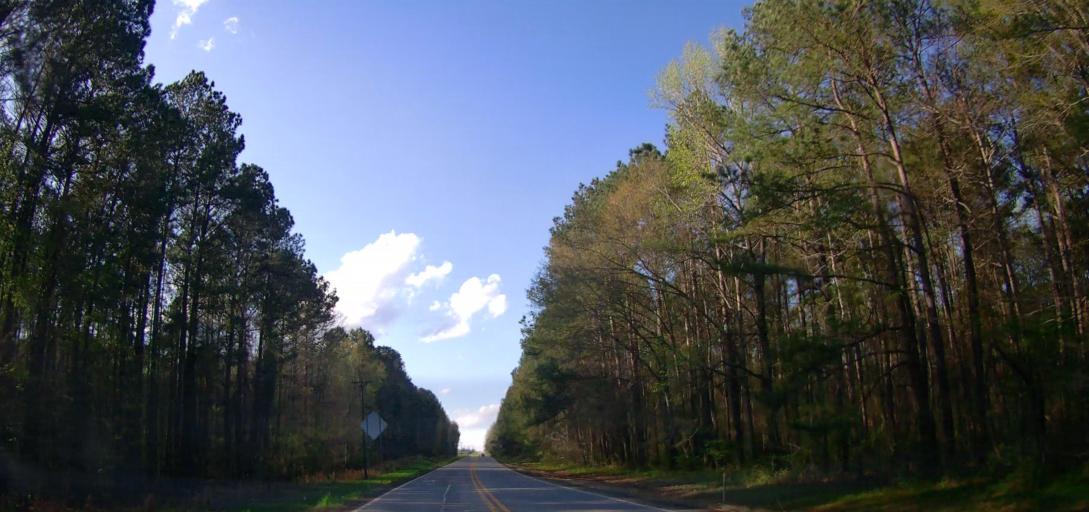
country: US
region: Georgia
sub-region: Putnam County
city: Eatonton
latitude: 33.1843
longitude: -83.4134
